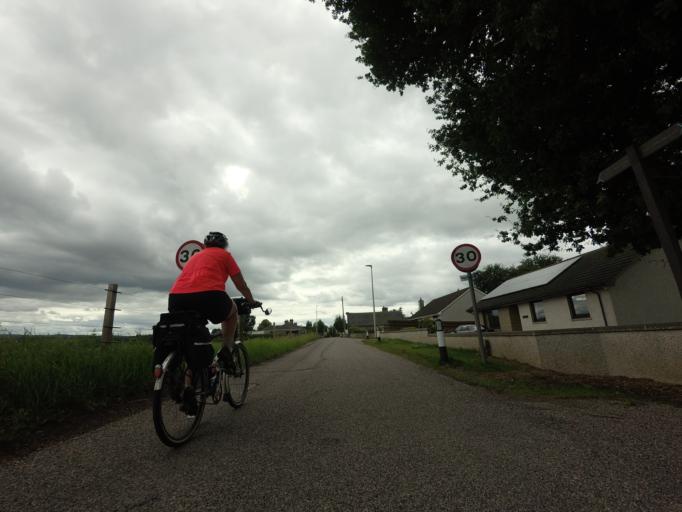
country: GB
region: Scotland
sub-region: Moray
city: Forres
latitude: 57.6073
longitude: -3.6915
